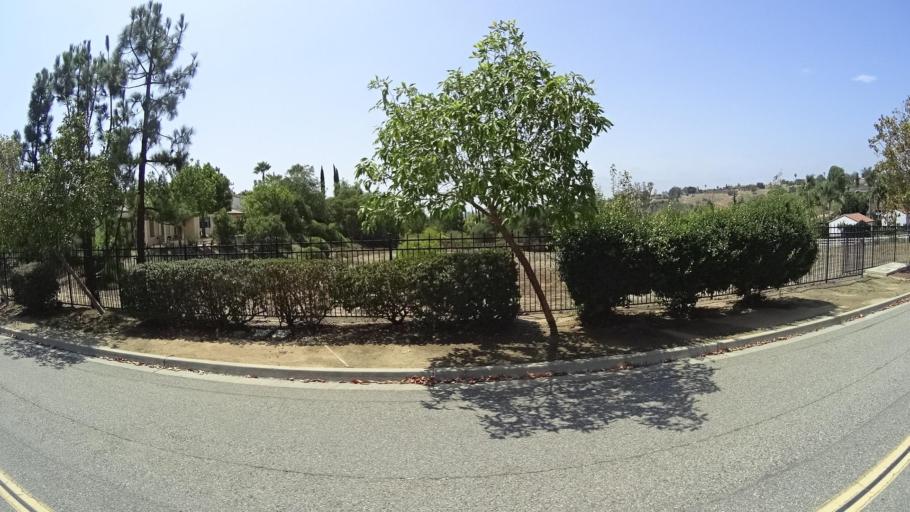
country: US
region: California
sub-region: San Diego County
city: Bonsall
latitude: 33.3252
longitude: -117.2133
